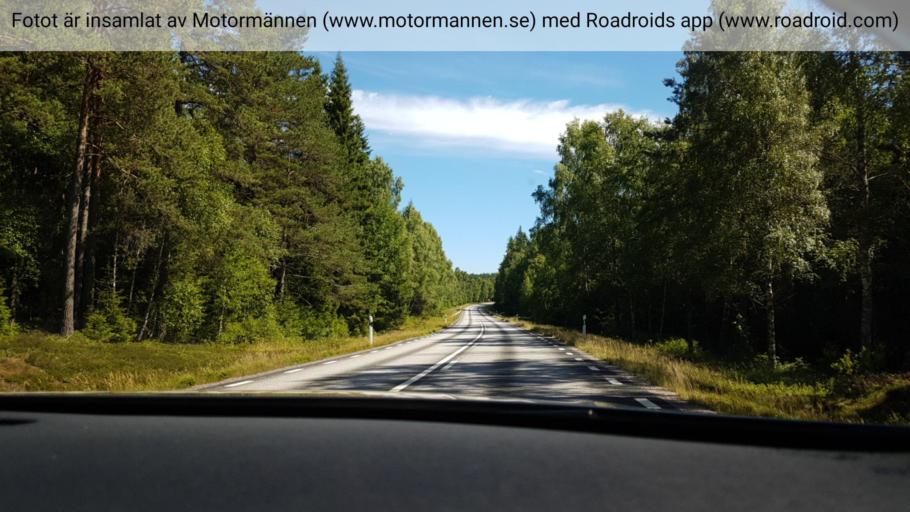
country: SE
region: Joenkoeping
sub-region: Gnosjo Kommun
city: Gnosjoe
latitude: 57.3544
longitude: 13.7544
